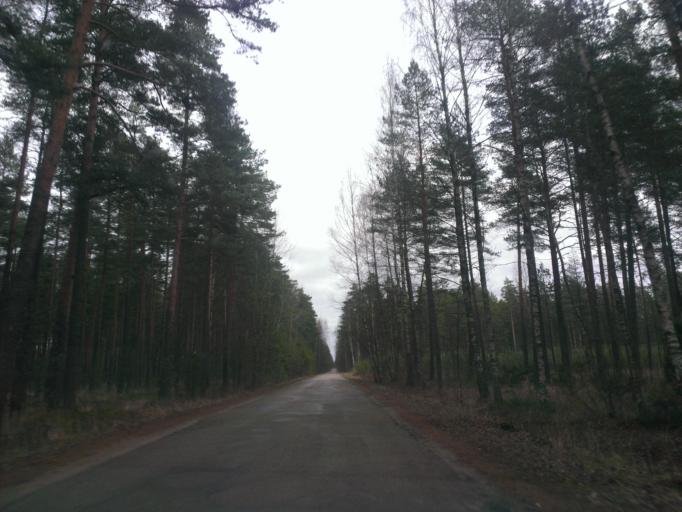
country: LV
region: Riga
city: Bergi
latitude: 57.0034
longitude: 24.3106
